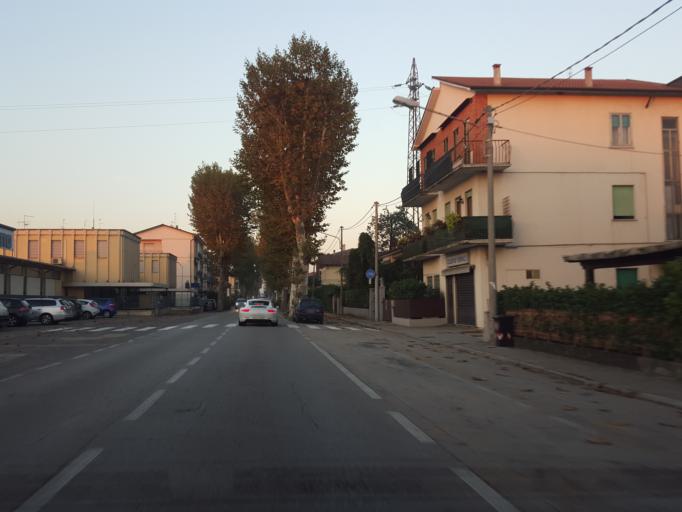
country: IT
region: Veneto
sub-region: Provincia di Vicenza
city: Vicenza
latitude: 45.5283
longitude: 11.5188
